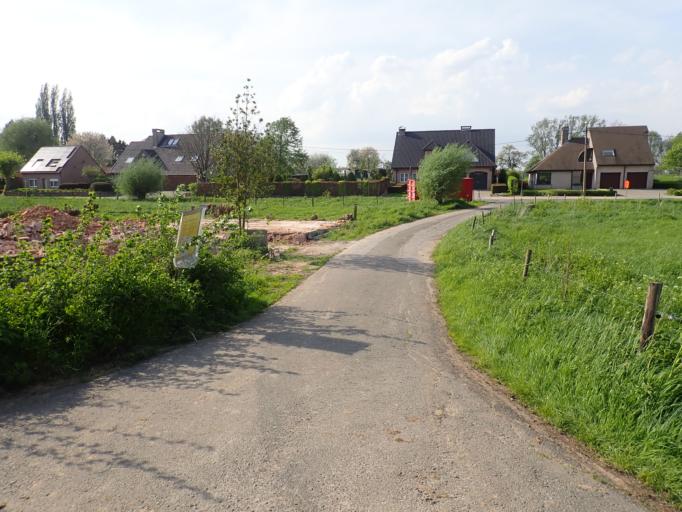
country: BE
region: Flanders
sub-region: Provincie Vlaams-Brabant
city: Wemmel
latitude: 50.9325
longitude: 4.2766
